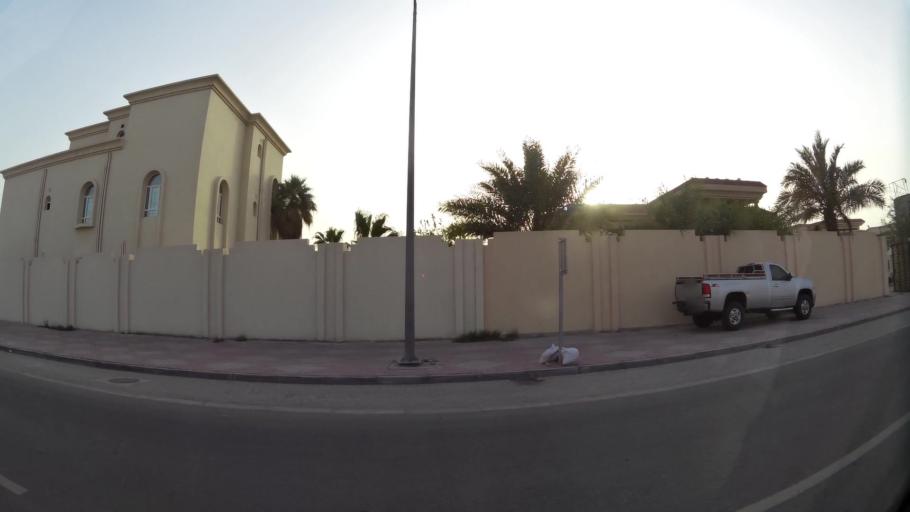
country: QA
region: Baladiyat ar Rayyan
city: Ar Rayyan
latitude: 25.2387
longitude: 51.4458
